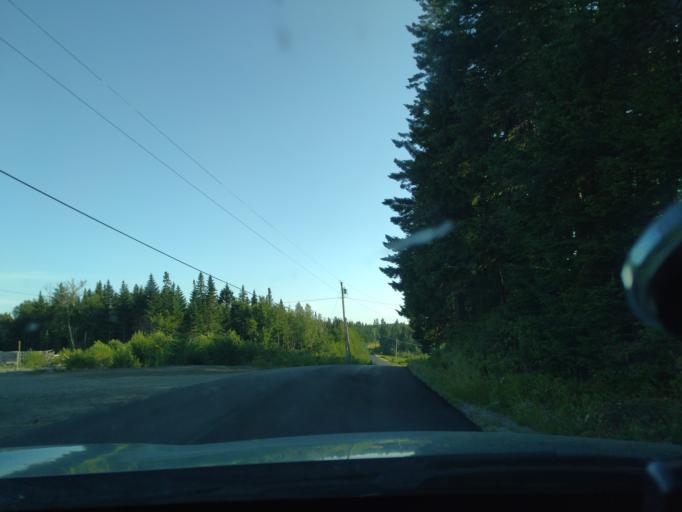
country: US
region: Maine
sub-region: Washington County
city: Machiasport
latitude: 44.6726
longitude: -67.1942
